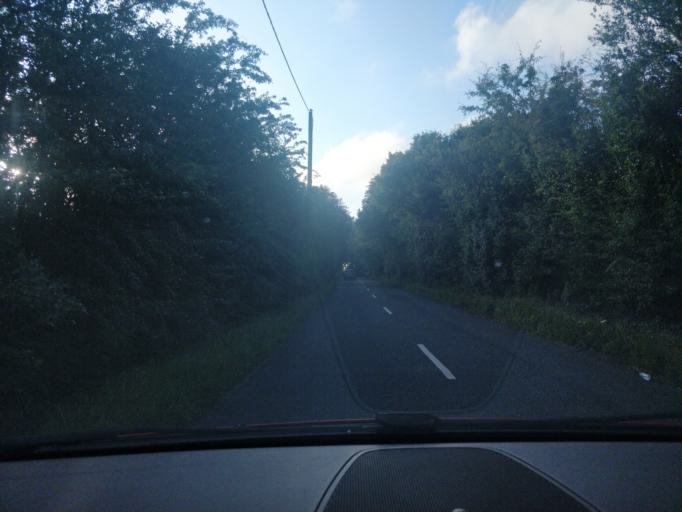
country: GB
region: England
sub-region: Lancashire
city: Skelmersdale
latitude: 53.5607
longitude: -2.7513
